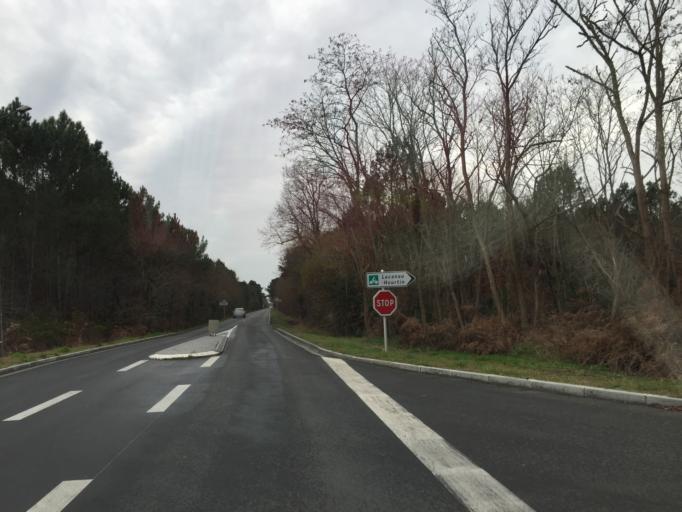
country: FR
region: Aquitaine
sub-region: Departement de la Gironde
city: Carcans
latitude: 45.0723
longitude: -1.0457
